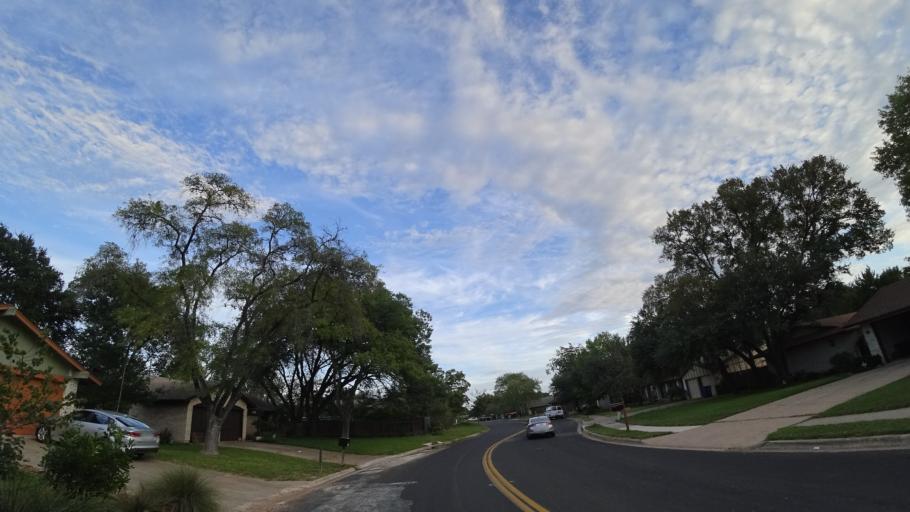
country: US
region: Texas
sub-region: Travis County
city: Austin
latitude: 30.2044
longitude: -97.7665
